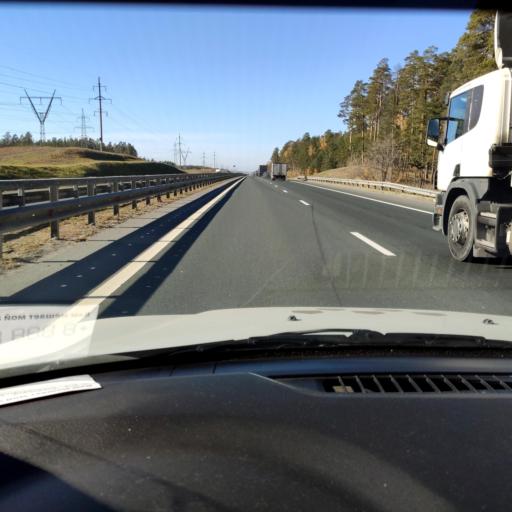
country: RU
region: Samara
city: Povolzhskiy
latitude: 53.5181
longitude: 49.7585
